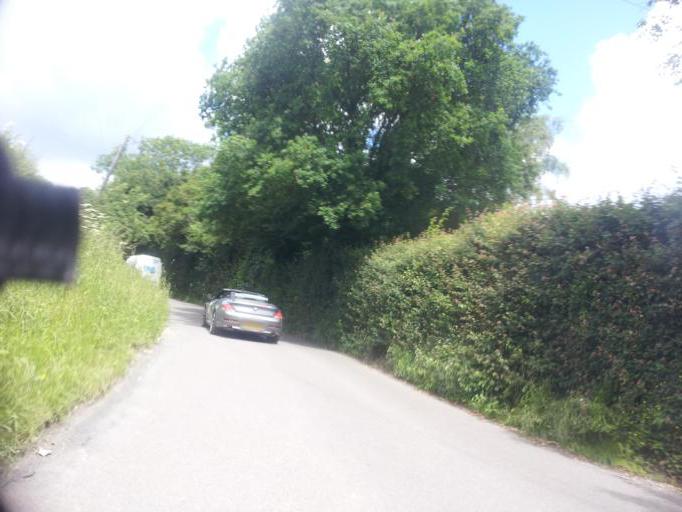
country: GB
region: England
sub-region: Kent
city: Meopham
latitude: 51.3204
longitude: 0.3492
